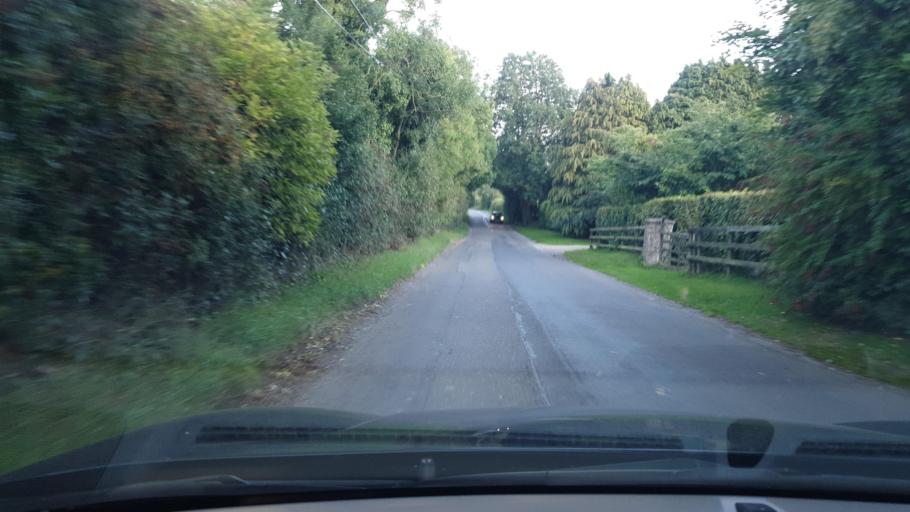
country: IE
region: Leinster
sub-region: An Mhi
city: Ashbourne
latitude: 53.5405
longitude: -6.3418
